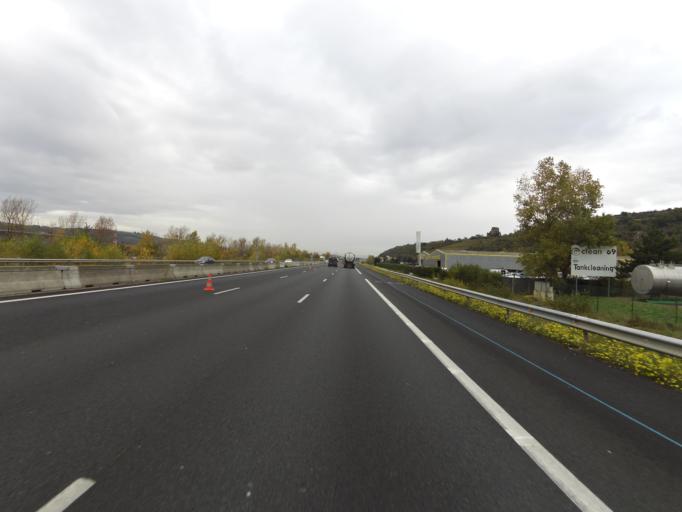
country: FR
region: Rhone-Alpes
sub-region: Departement de l'Isere
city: Seyssuel
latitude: 45.5544
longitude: 4.8270
